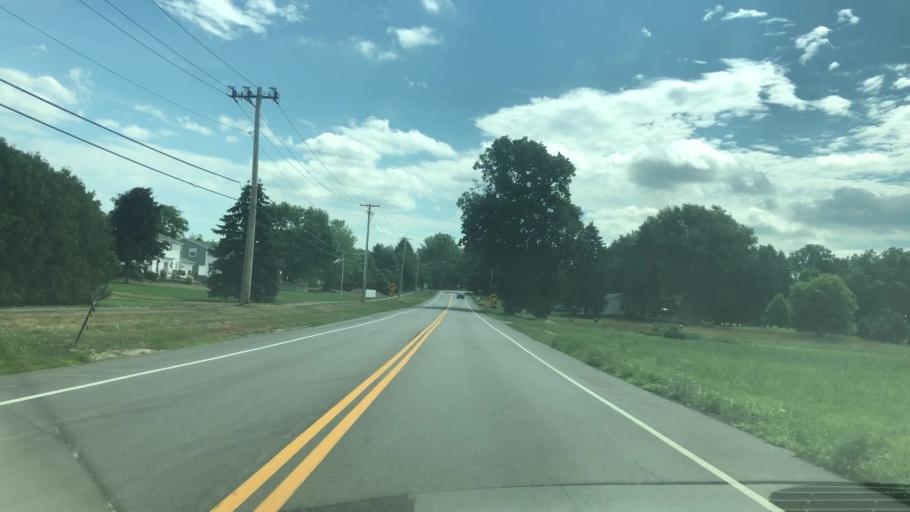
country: US
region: New York
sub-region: Monroe County
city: Fairport
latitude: 43.0794
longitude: -77.3961
